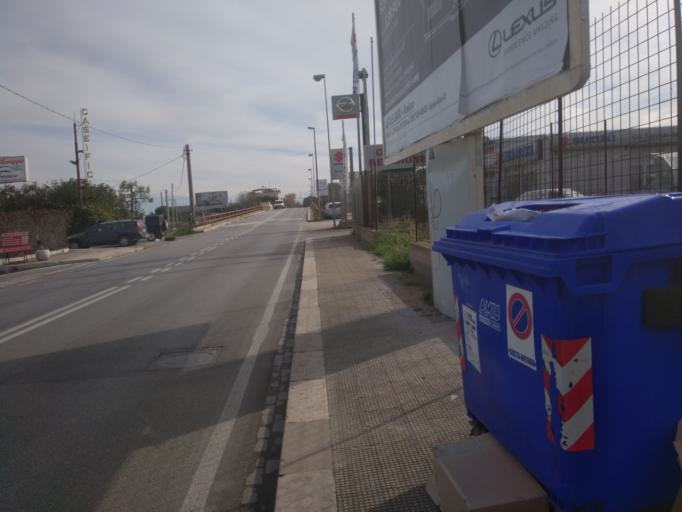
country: IT
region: Apulia
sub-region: Provincia di Bari
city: Bari
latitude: 41.1118
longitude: 16.9016
